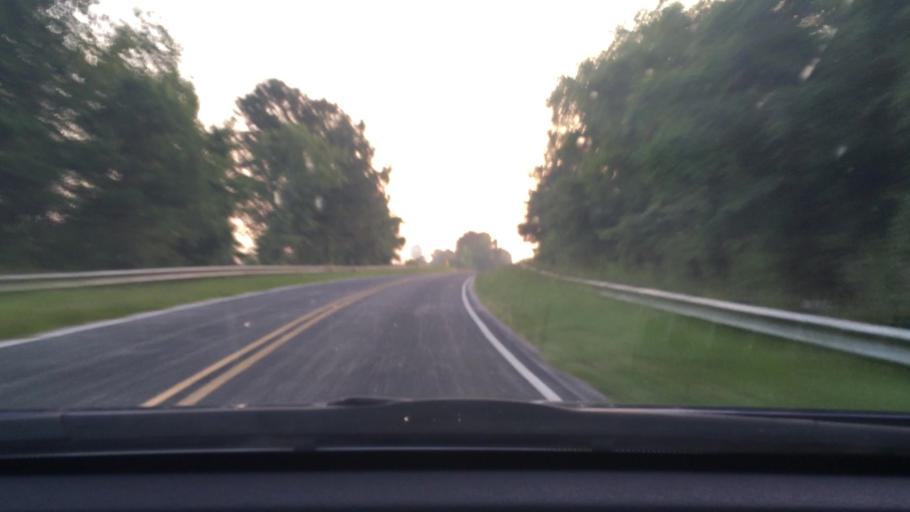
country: US
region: South Carolina
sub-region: Lee County
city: Bishopville
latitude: 34.1928
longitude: -80.1409
